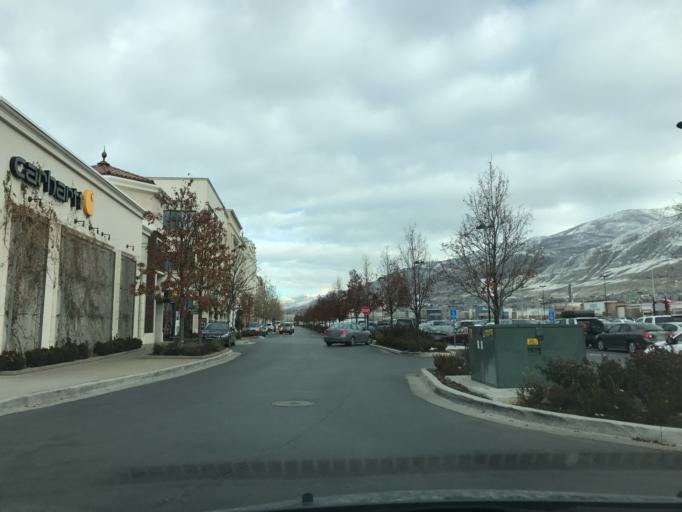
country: US
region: Utah
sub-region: Davis County
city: Farmington
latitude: 40.9824
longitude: -111.9056
